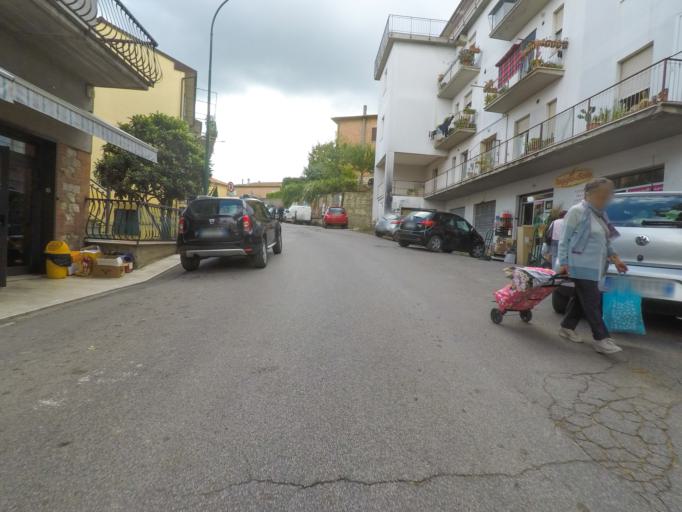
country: IT
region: Tuscany
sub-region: Provincia di Siena
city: Montepulciano
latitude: 43.0991
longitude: 11.7874
